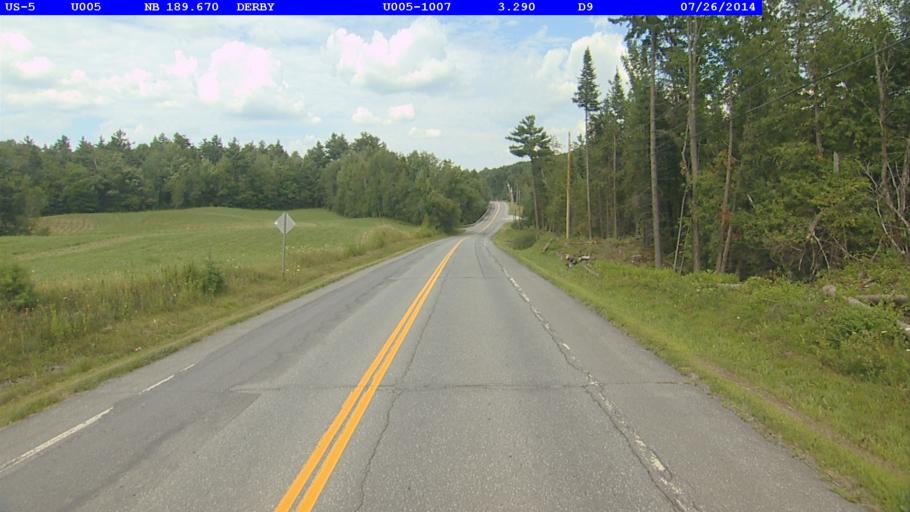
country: US
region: Vermont
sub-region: Orleans County
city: Newport
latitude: 44.9713
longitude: -72.1196
